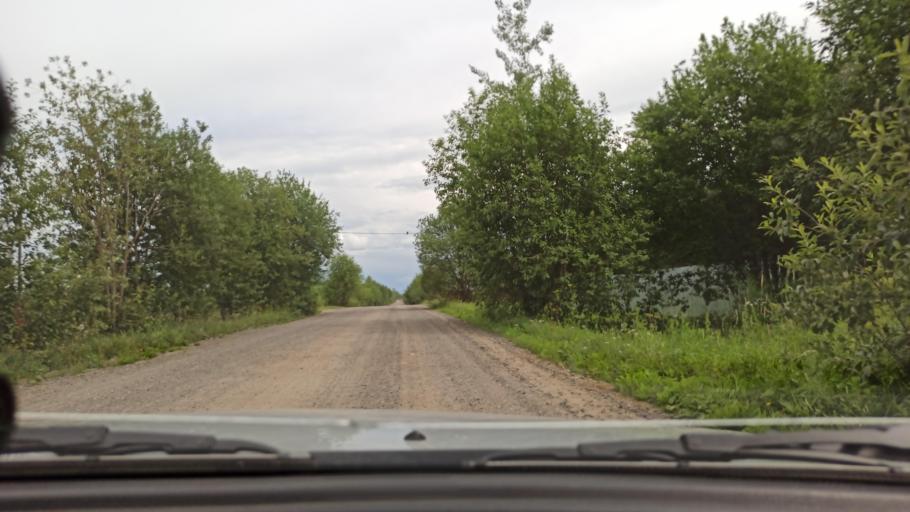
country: RU
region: Vologda
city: Molochnoye
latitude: 59.3680
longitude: 39.6747
